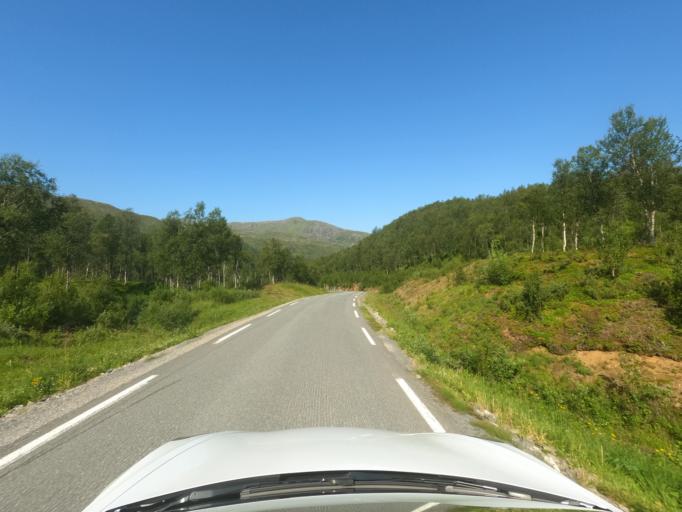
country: NO
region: Troms
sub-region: Skanland
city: Evenskjer
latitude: 68.3286
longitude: 16.5551
